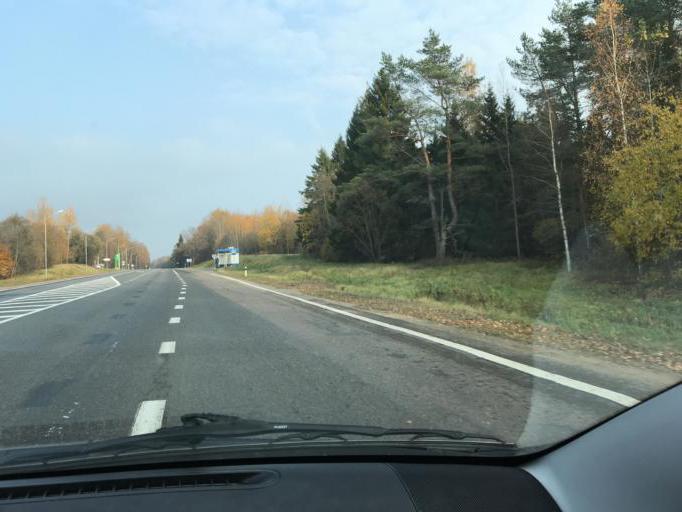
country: BY
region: Vitebsk
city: Syanno
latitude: 55.1188
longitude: 29.7769
